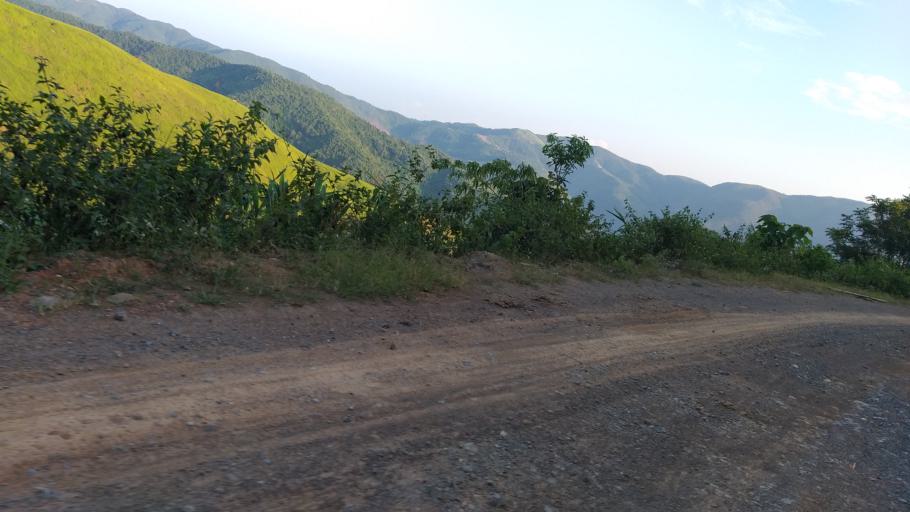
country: LA
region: Phongsali
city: Khoa
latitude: 21.1910
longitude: 102.5590
